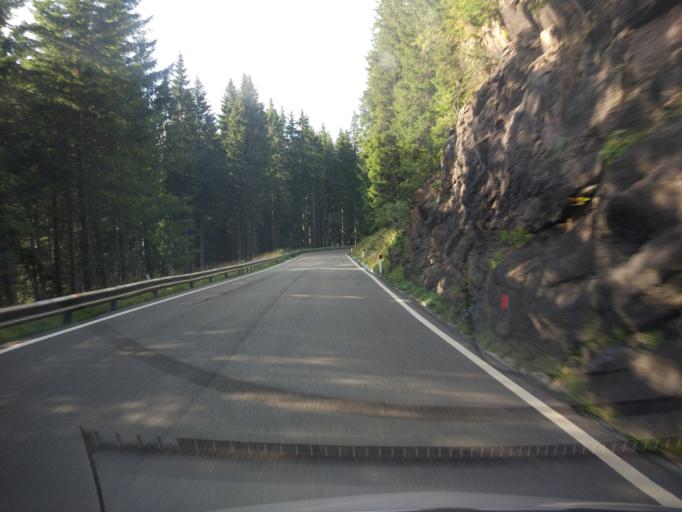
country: IT
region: Veneto
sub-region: Provincia di Belluno
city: Falcade Alto
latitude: 46.2979
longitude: 11.7646
